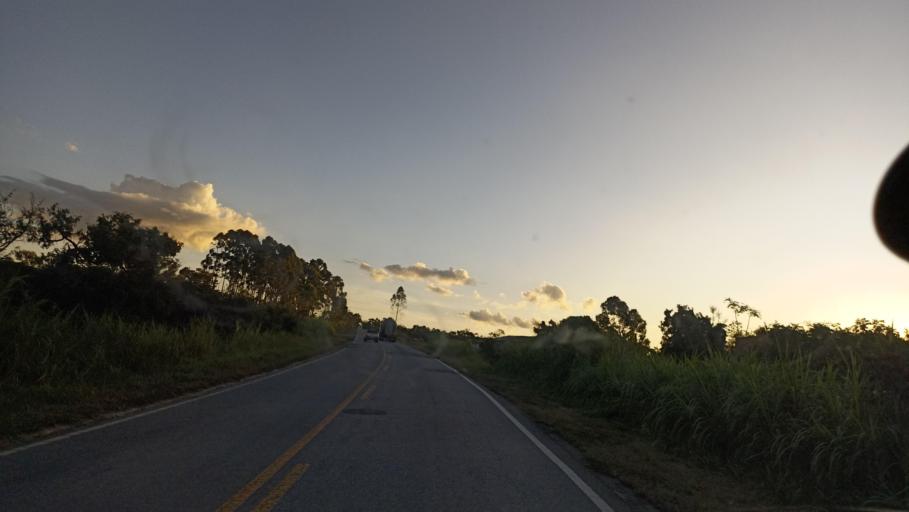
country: BR
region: Minas Gerais
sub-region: Sao Joao Del Rei
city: Sao Joao del Rei
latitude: -21.2357
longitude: -44.3946
